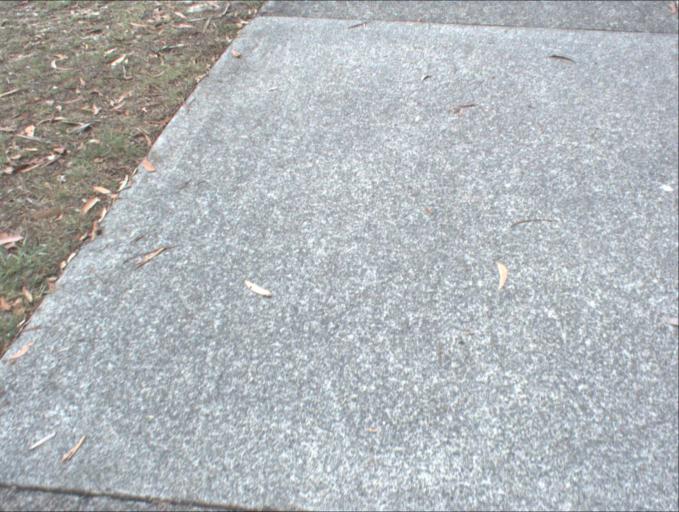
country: AU
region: Queensland
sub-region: Logan
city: Springwood
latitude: -27.6157
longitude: 153.1307
